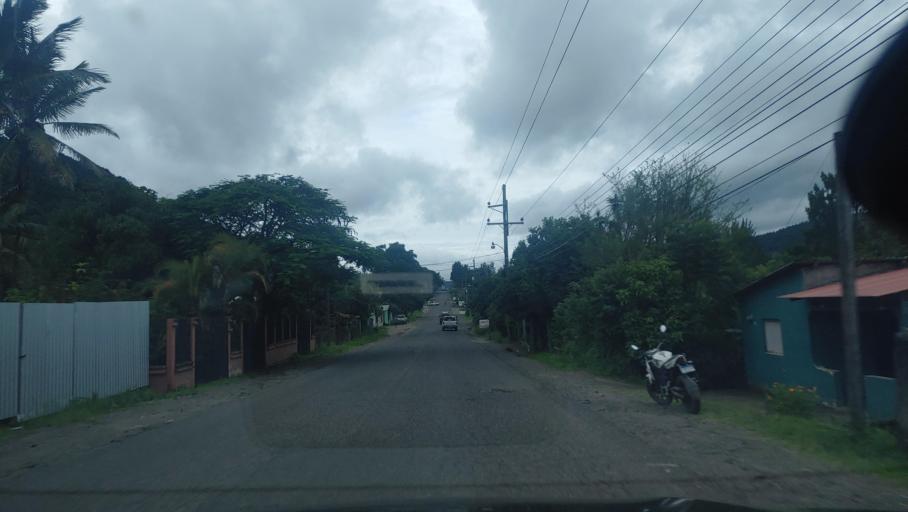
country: HN
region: Choluteca
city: San Marcos de Colon
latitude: 13.3757
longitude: -86.9008
